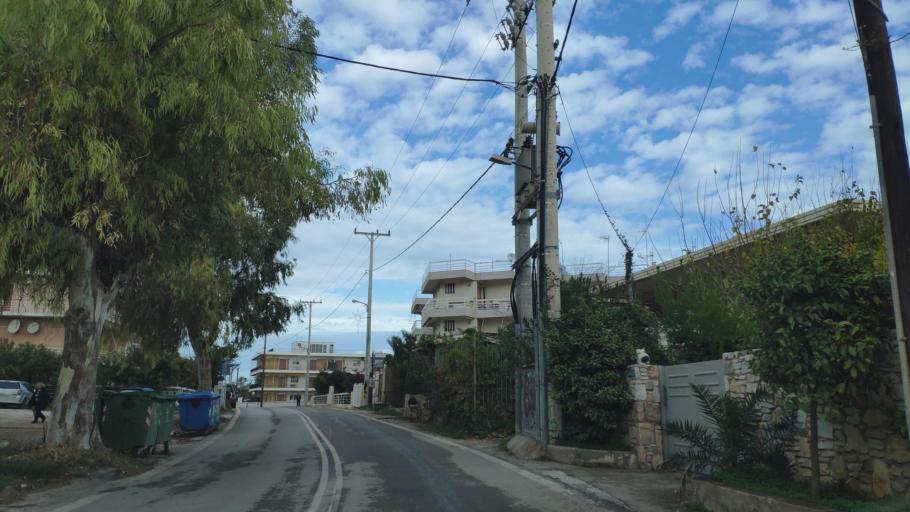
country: GR
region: Attica
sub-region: Nomarchia Anatolikis Attikis
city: Artemida
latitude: 37.9338
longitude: 24.0118
